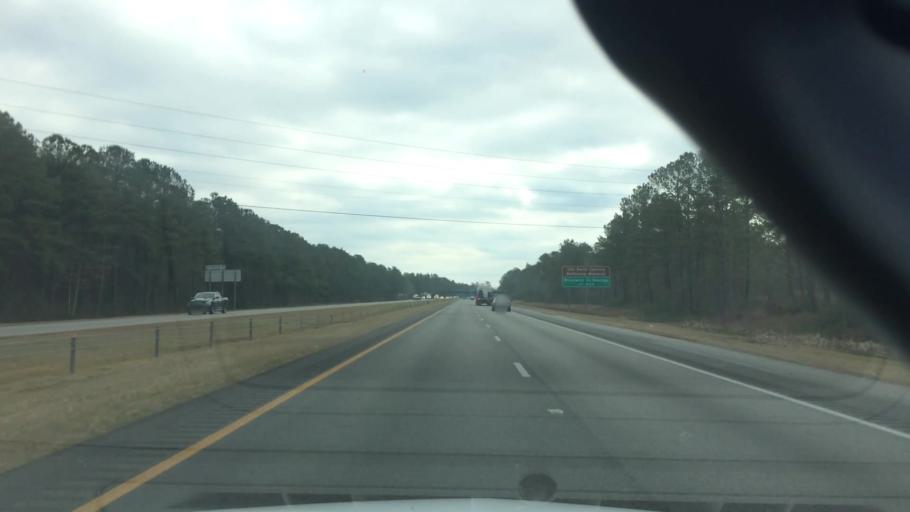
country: US
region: North Carolina
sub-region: New Hanover County
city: Skippers Corner
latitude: 34.3343
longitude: -77.8763
